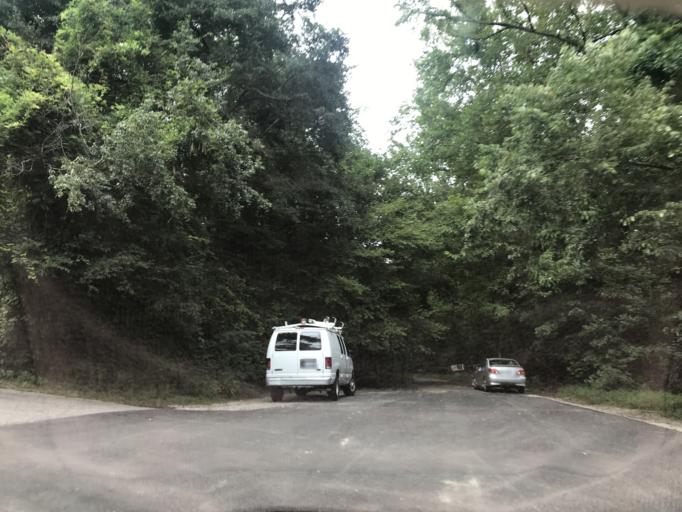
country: US
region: North Carolina
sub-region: Wake County
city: Knightdale
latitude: 35.7994
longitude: -78.5420
